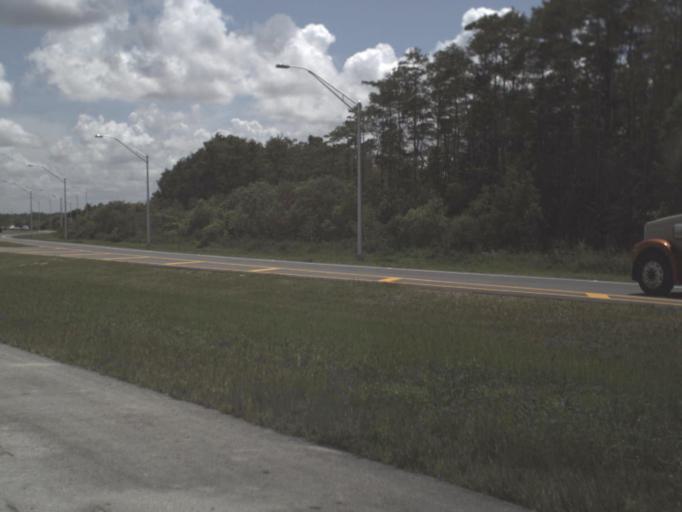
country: US
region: Florida
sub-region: Collier County
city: Immokalee
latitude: 26.1682
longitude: -81.0825
